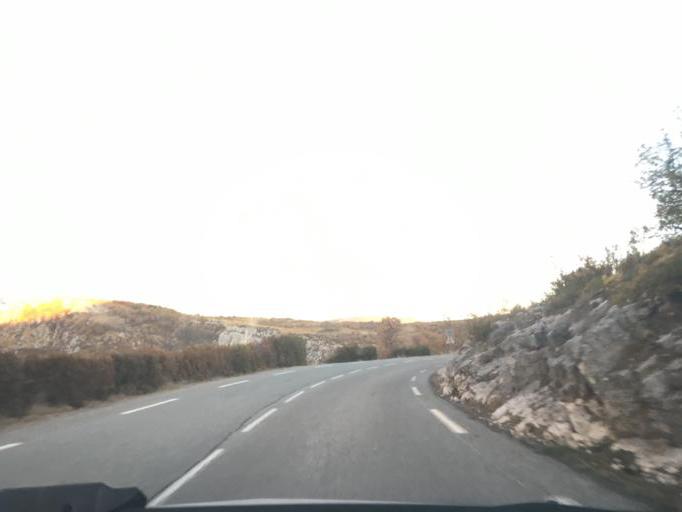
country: FR
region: Provence-Alpes-Cote d'Azur
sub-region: Departement du Var
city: Bargemon
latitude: 43.7060
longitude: 6.5078
